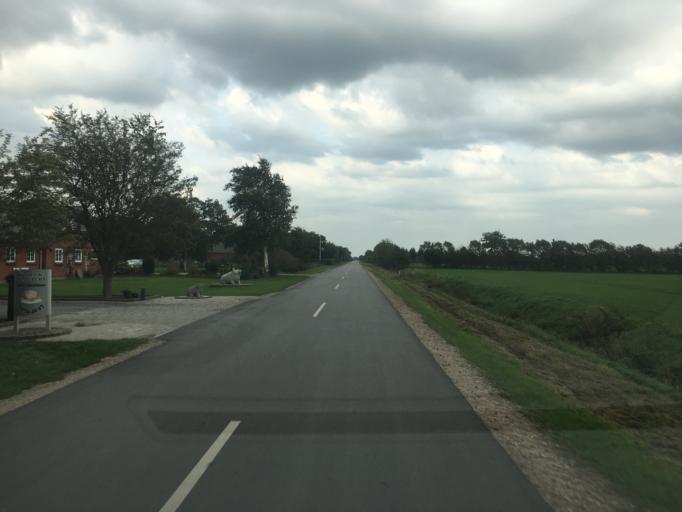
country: DK
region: South Denmark
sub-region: Tonder Kommune
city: Logumkloster
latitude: 55.0625
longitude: 9.0309
